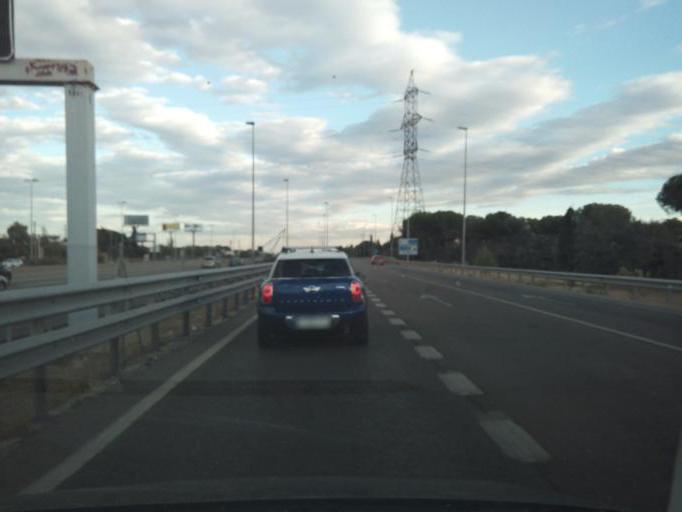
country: ES
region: Madrid
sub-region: Provincia de Madrid
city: Las Rozas de Madrid
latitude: 40.5149
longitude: -3.8832
